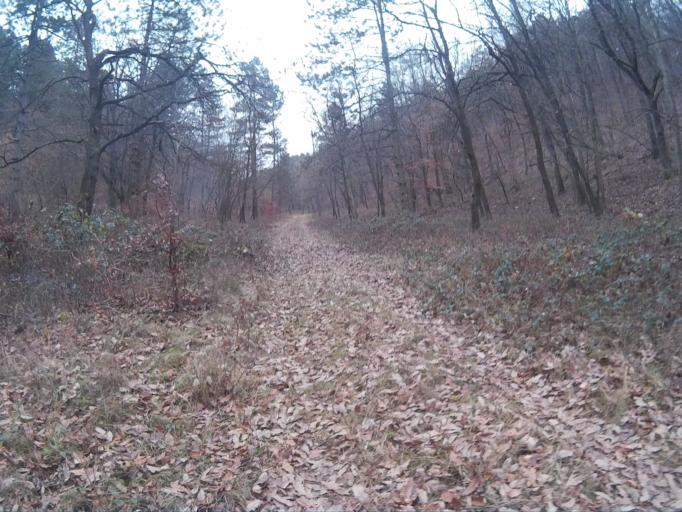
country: HU
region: Veszprem
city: Tapolca
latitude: 46.9725
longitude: 17.4827
